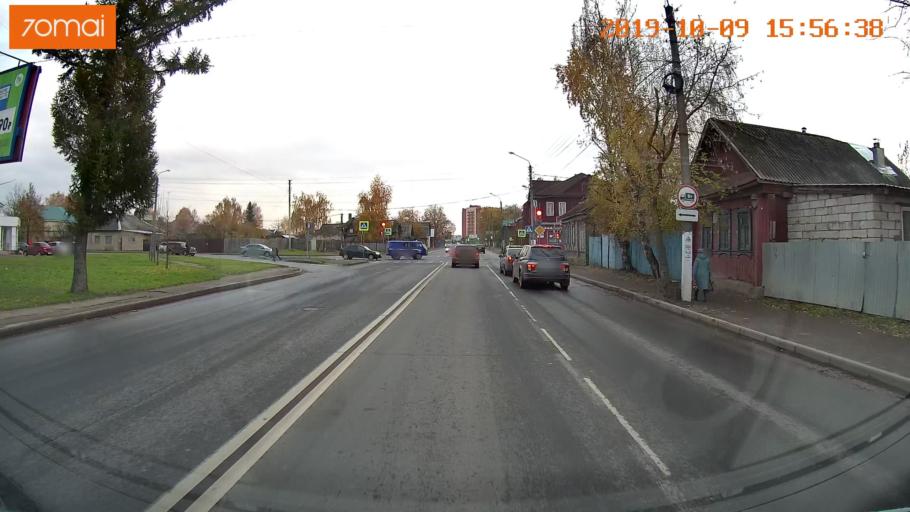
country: RU
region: Kostroma
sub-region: Kostromskoy Rayon
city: Kostroma
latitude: 57.7741
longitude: 40.9464
